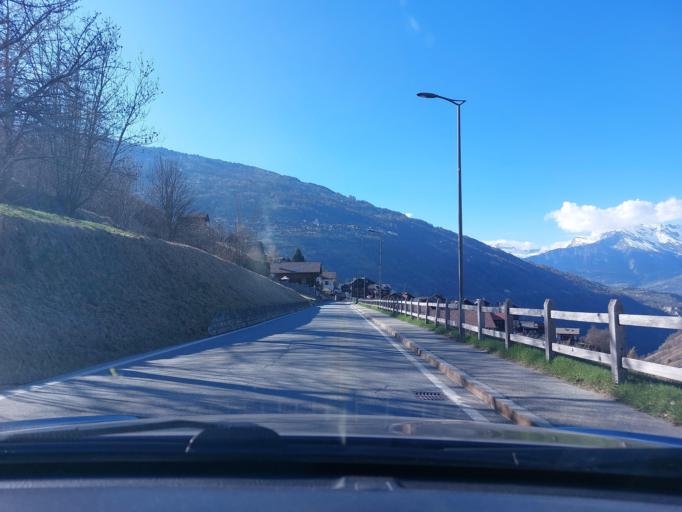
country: CH
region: Valais
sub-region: Herens District
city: Heremence
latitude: 46.1702
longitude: 7.4255
